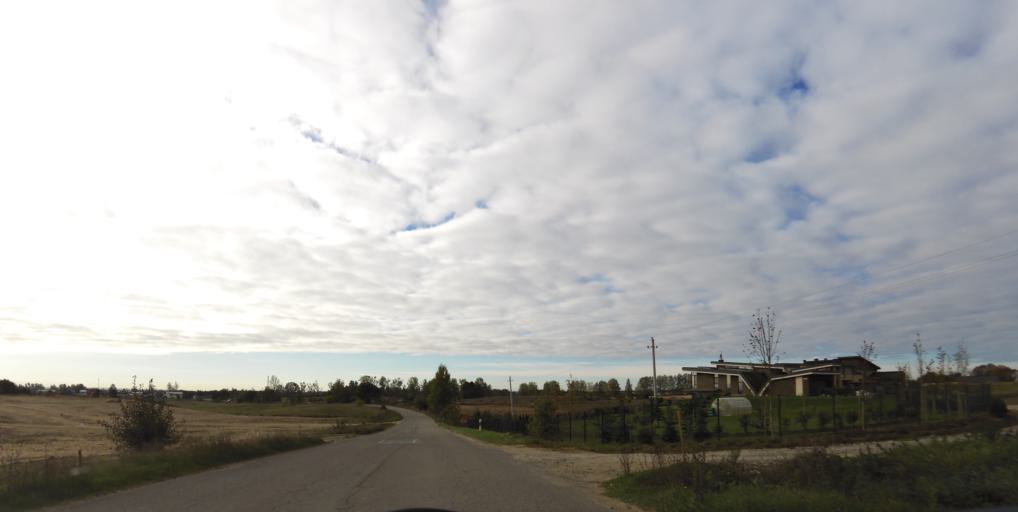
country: LT
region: Vilnius County
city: Pilaite
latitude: 54.7270
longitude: 25.1529
